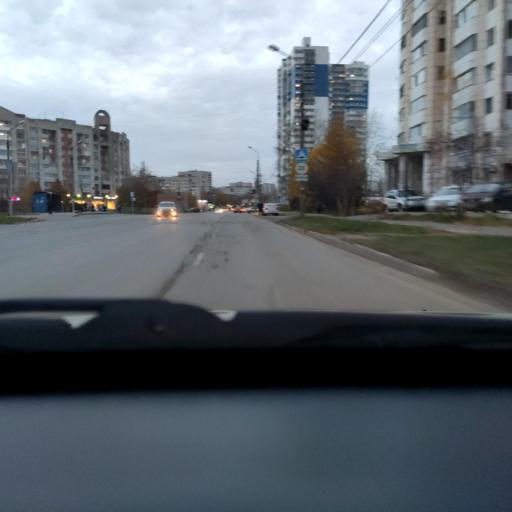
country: RU
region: Perm
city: Perm
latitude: 57.9691
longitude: 56.2268
